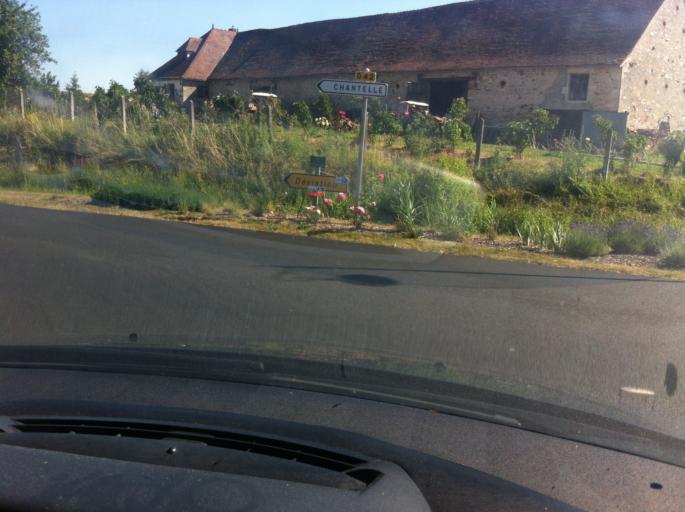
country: FR
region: Auvergne
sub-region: Departement de l'Allier
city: Chantelle
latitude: 46.2409
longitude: 3.1108
